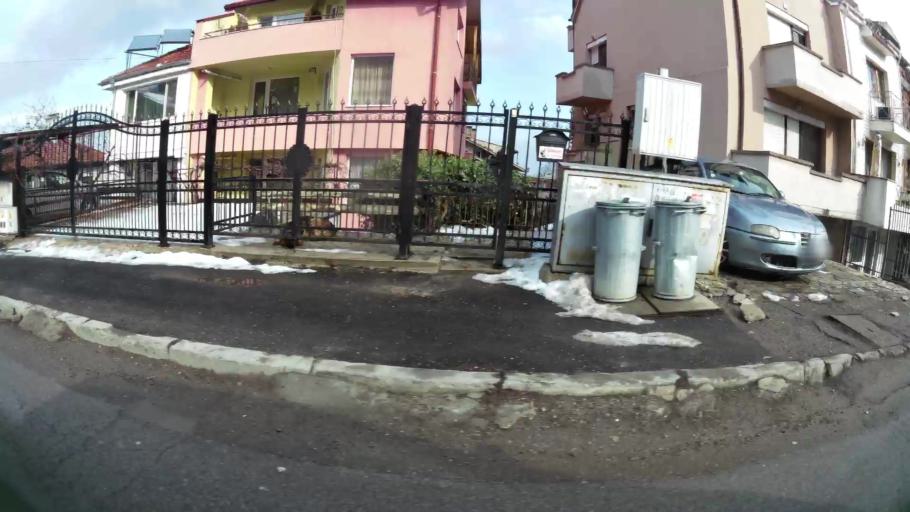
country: BG
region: Sofia-Capital
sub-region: Stolichna Obshtina
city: Sofia
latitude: 42.6479
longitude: 23.2651
